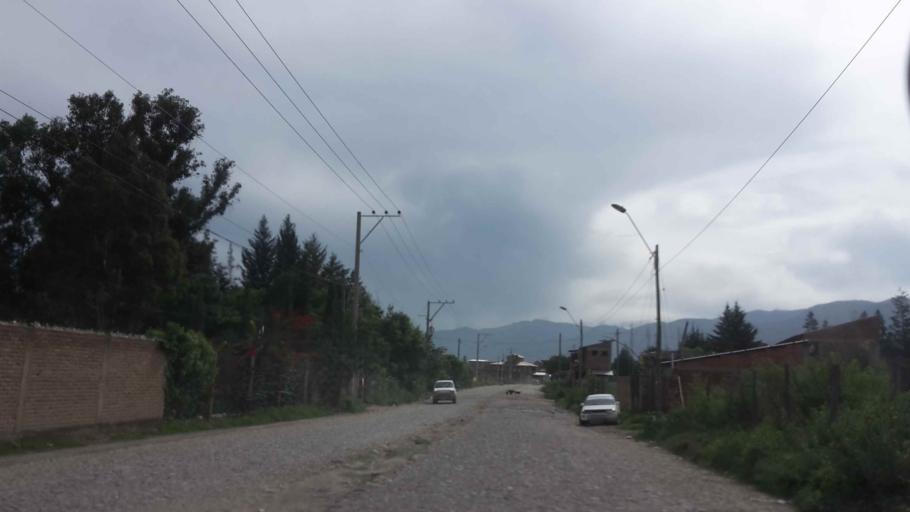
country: BO
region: Cochabamba
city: Cochabamba
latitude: -17.3355
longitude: -66.2562
